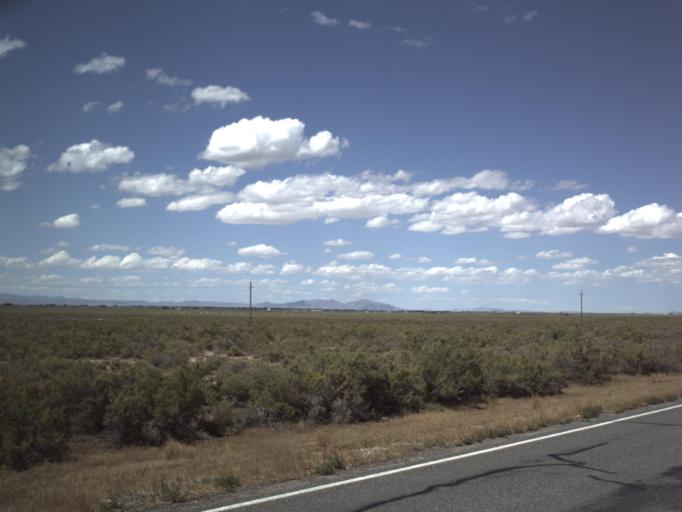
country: US
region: Utah
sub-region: Millard County
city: Delta
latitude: 39.3164
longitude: -112.4798
